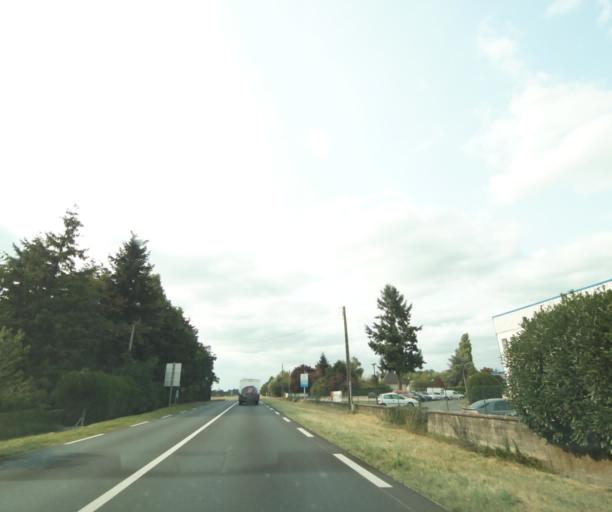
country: FR
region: Centre
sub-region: Departement d'Indre-et-Loire
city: Esvres
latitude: 47.2931
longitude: 0.8072
